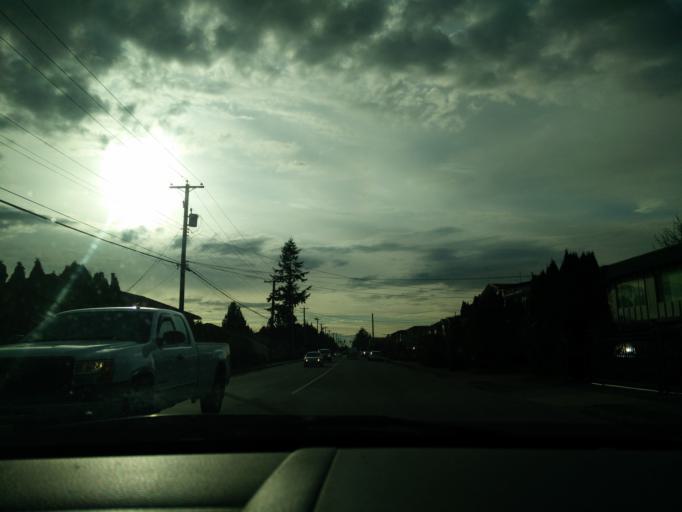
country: CA
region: British Columbia
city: Burnaby
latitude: 49.2150
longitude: -122.9901
